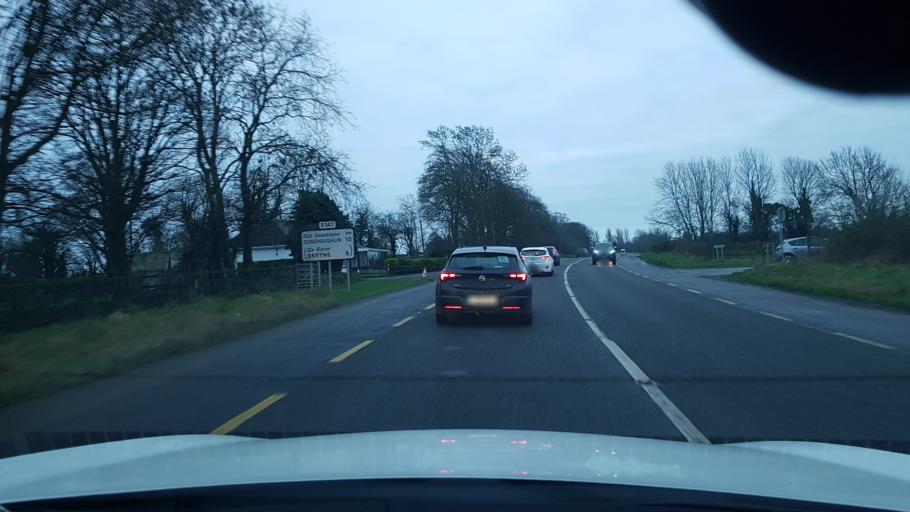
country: IE
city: Kentstown
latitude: 53.5975
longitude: -6.6097
